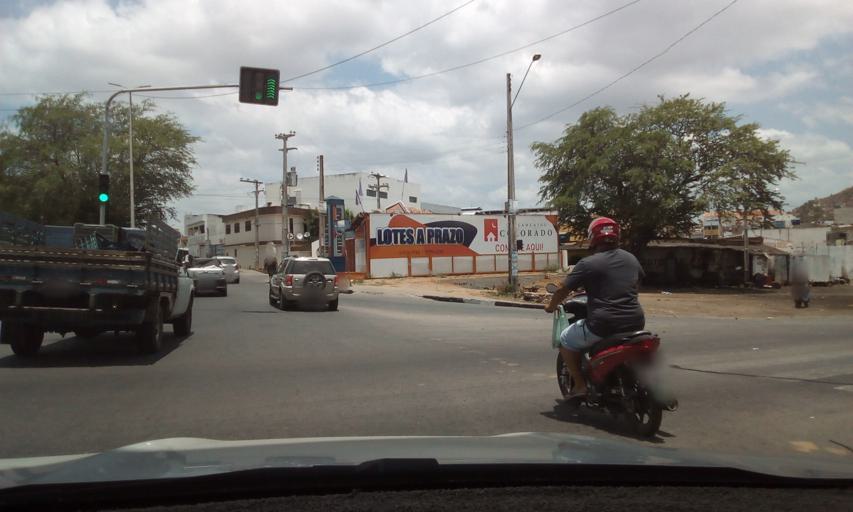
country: BR
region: Pernambuco
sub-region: Caruaru
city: Caruaru
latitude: -8.2761
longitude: -35.9819
